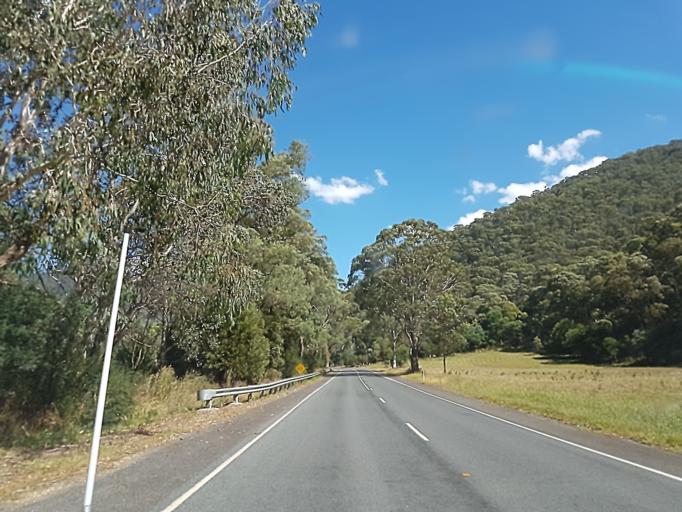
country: AU
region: Victoria
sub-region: Alpine
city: Mount Beauty
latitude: -36.8430
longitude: 147.0784
